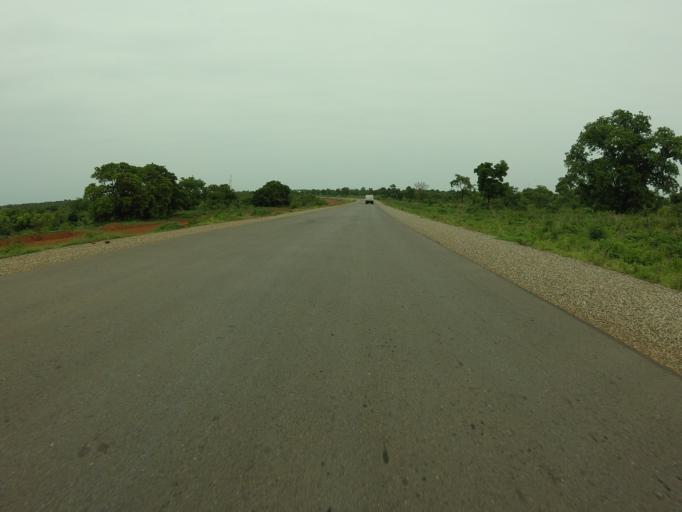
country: GH
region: Northern
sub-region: Yendi
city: Yendi
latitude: 9.2952
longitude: 0.0191
